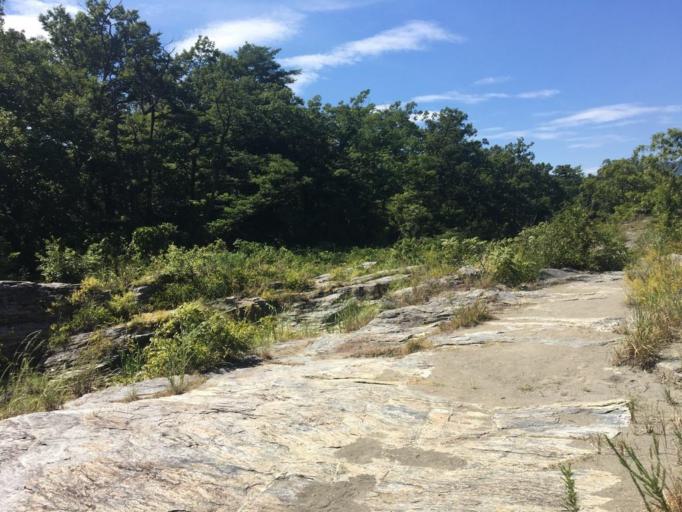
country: JP
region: Saitama
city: Yorii
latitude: 36.0927
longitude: 139.1165
